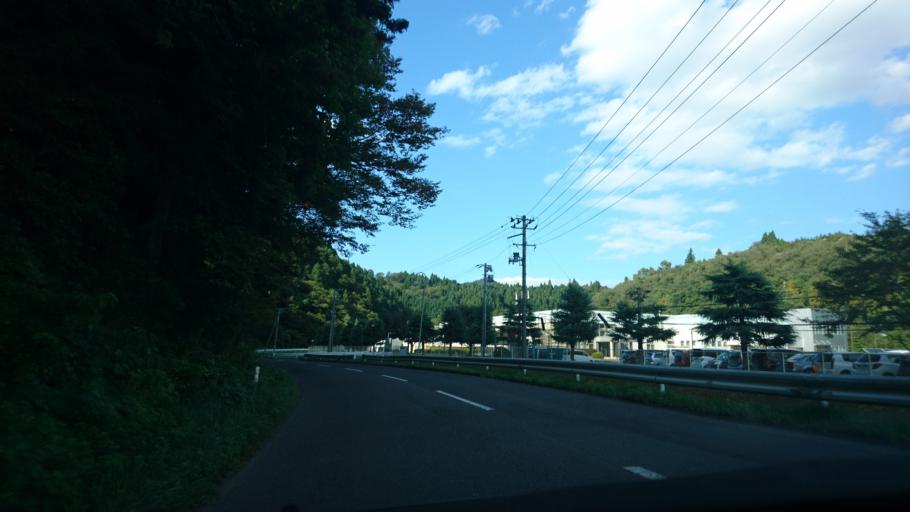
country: JP
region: Iwate
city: Ichinoseki
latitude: 38.8525
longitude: 141.3033
